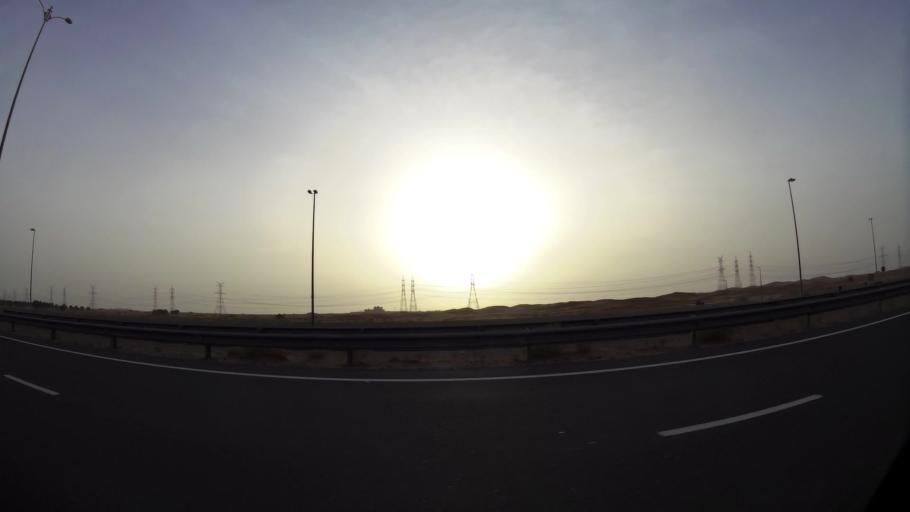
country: OM
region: Al Buraimi
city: Al Buraymi
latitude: 24.2913
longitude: 55.7368
